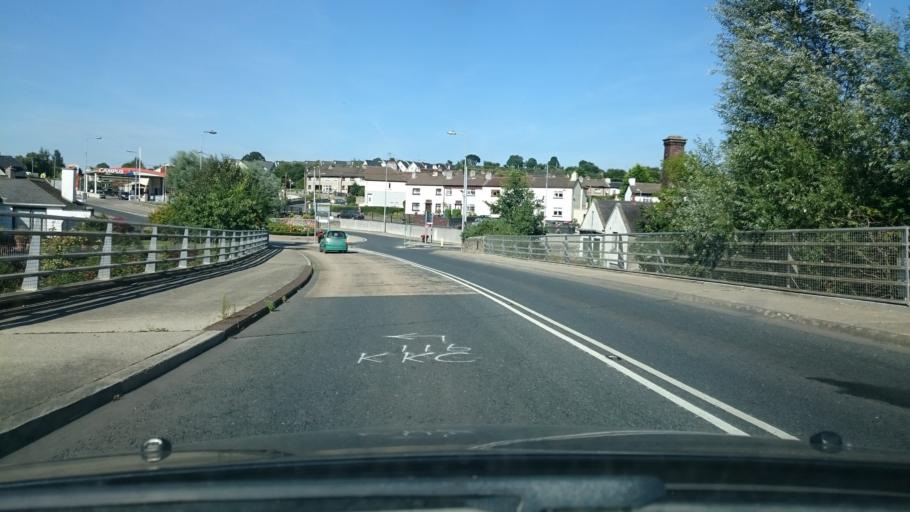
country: IE
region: Leinster
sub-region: Kilkenny
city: Graiguenamanagh
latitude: 52.5435
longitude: -6.9598
